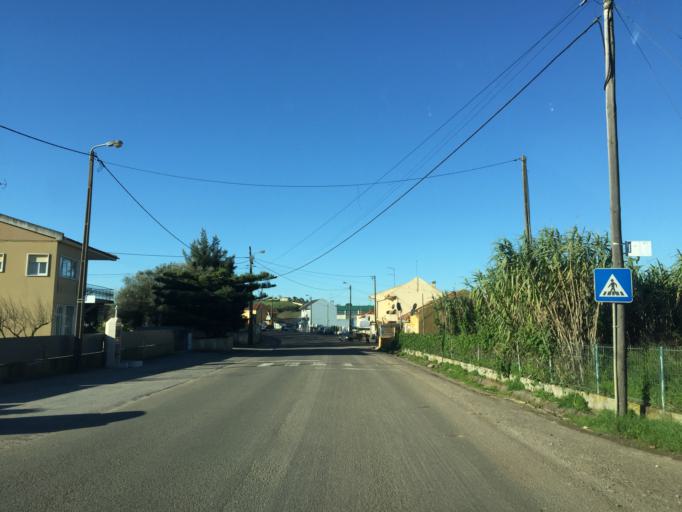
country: PT
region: Lisbon
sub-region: Sintra
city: Pero Pinheiro
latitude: 38.8696
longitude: -9.2959
